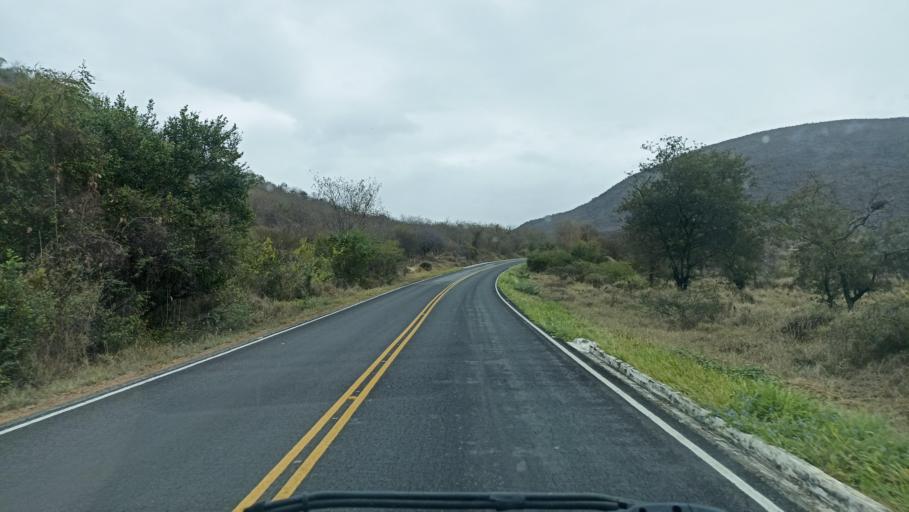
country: BR
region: Bahia
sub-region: Andarai
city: Vera Cruz
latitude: -13.0482
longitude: -40.7796
